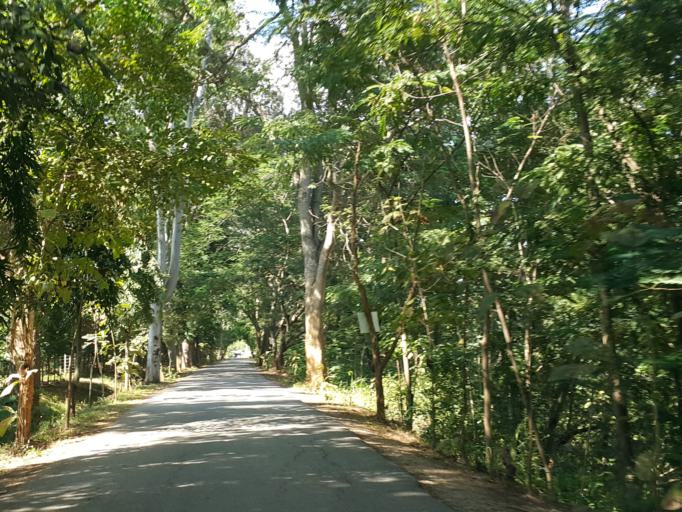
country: TH
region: Chiang Mai
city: San Sai
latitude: 18.9118
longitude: 98.9413
